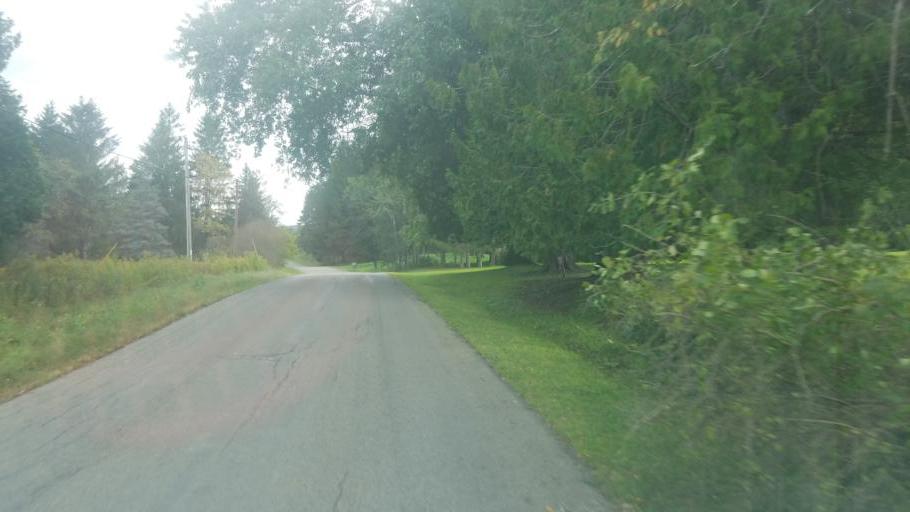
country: US
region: New York
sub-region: Cattaraugus County
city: Weston Mills
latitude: 42.1150
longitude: -78.3166
